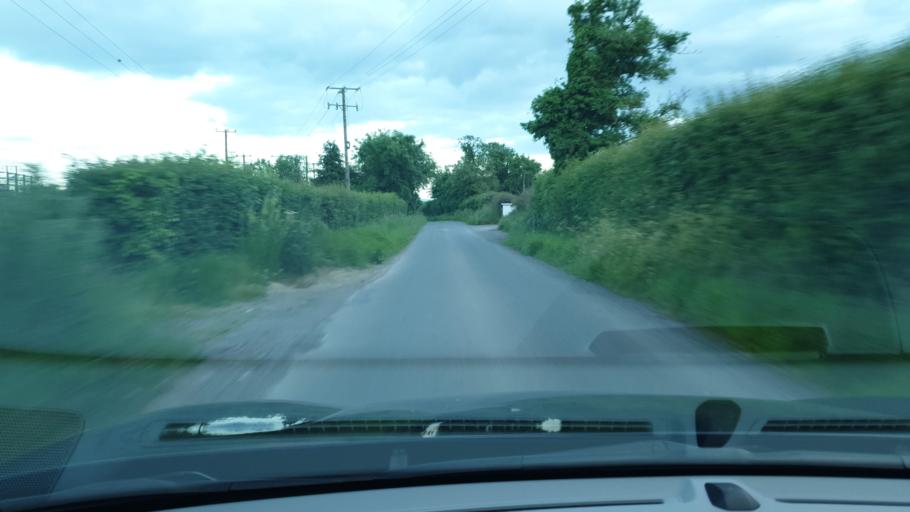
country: IE
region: Leinster
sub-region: An Mhi
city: Ashbourne
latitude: 53.4915
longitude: -6.3709
